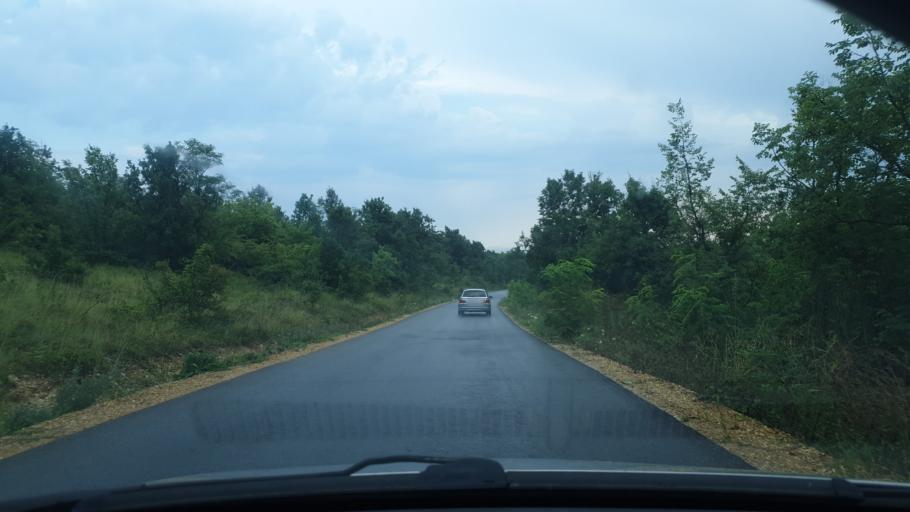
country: RS
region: Central Serbia
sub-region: Sumadijski Okrug
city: Kragujevac
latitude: 44.0555
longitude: 20.7830
